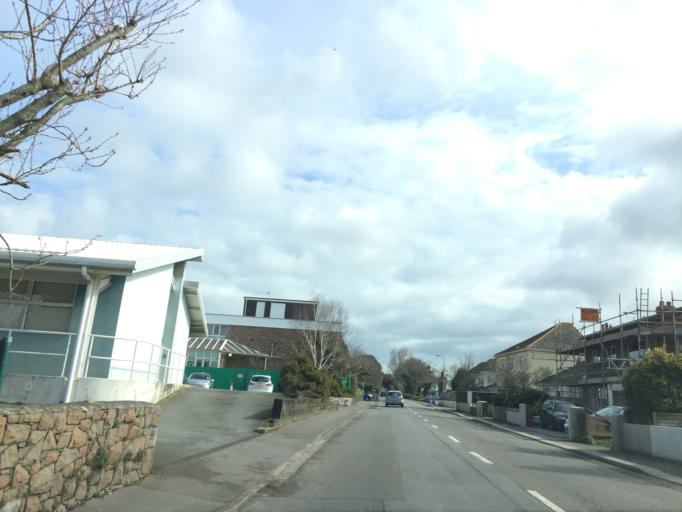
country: JE
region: St Helier
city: Saint Helier
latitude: 49.1991
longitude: -2.0797
